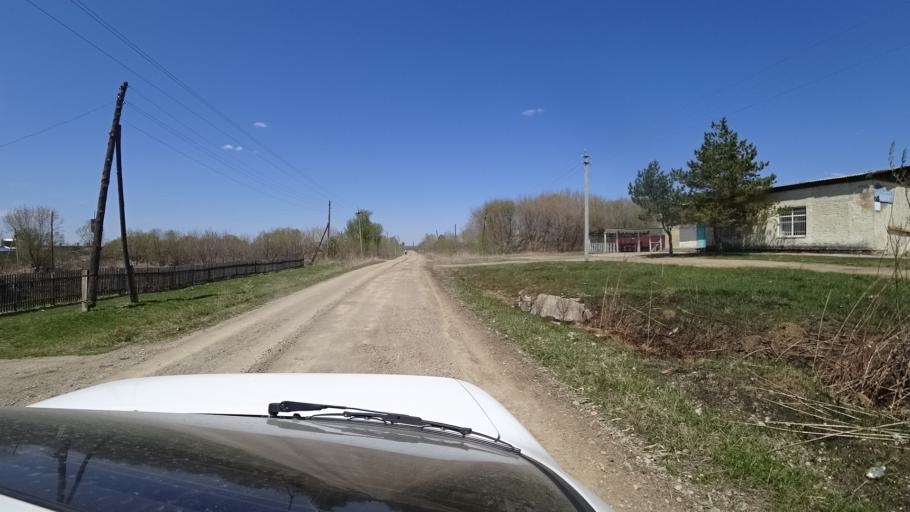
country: RU
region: Primorskiy
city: Lazo
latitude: 45.7966
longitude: 133.7650
